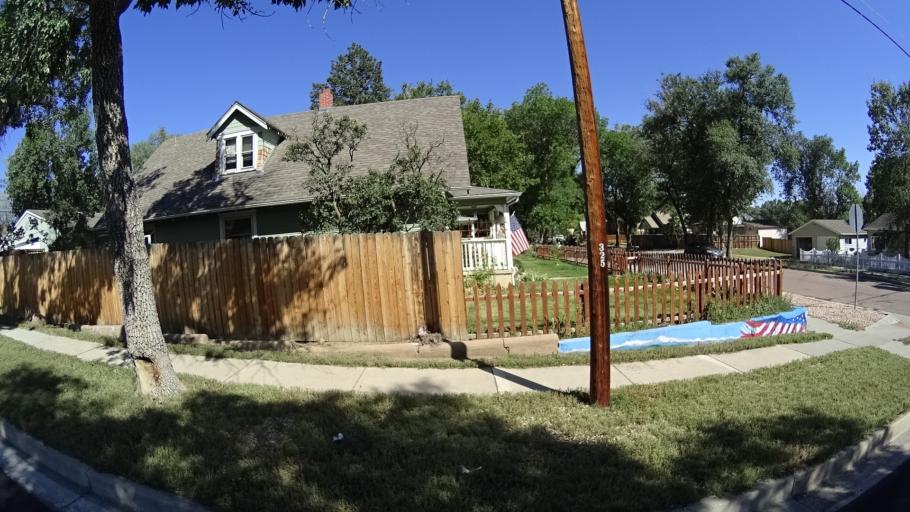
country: US
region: Colorado
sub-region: El Paso County
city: Colorado Springs
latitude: 38.8470
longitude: -104.8538
